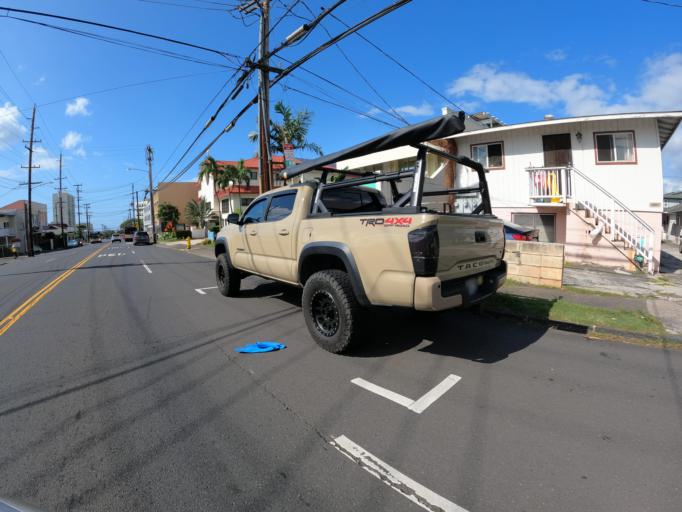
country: US
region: Hawaii
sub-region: Honolulu County
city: Honolulu
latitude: 21.3228
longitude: -157.8586
